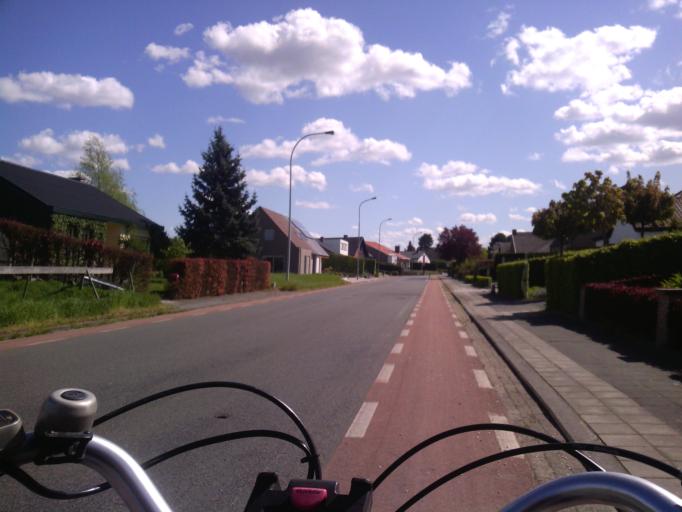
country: BE
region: Flanders
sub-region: Provincie West-Vlaanderen
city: Wevelgem
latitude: 50.7995
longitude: 3.1972
